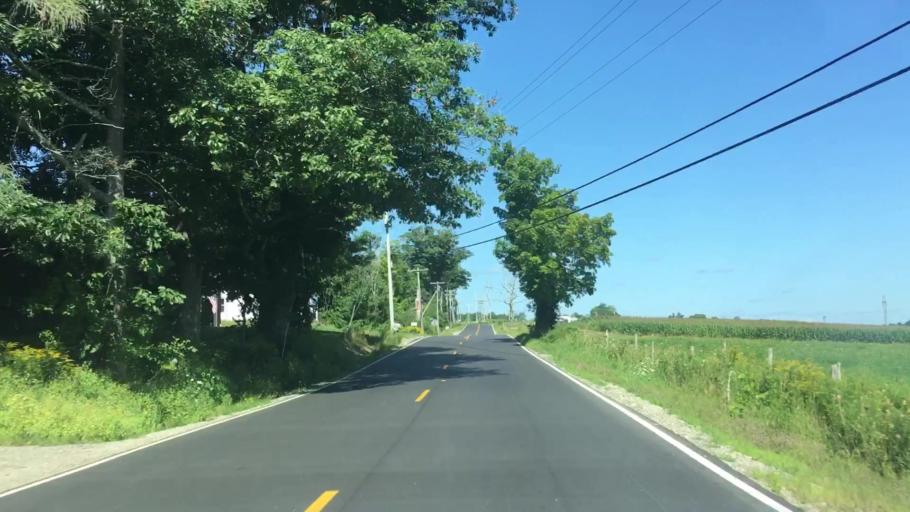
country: US
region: Maine
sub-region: Sagadahoc County
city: Topsham
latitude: 43.9555
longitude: -69.9732
